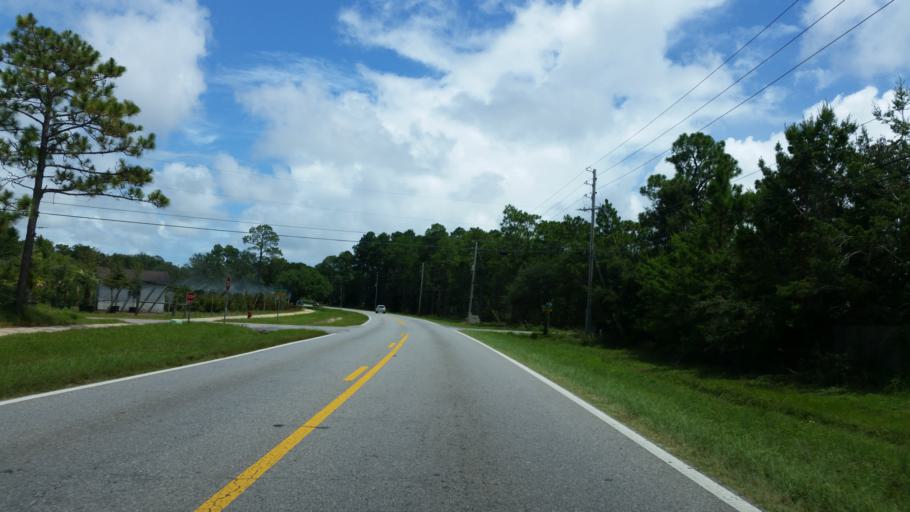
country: US
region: Florida
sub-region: Santa Rosa County
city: Holley
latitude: 30.4357
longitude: -86.9163
